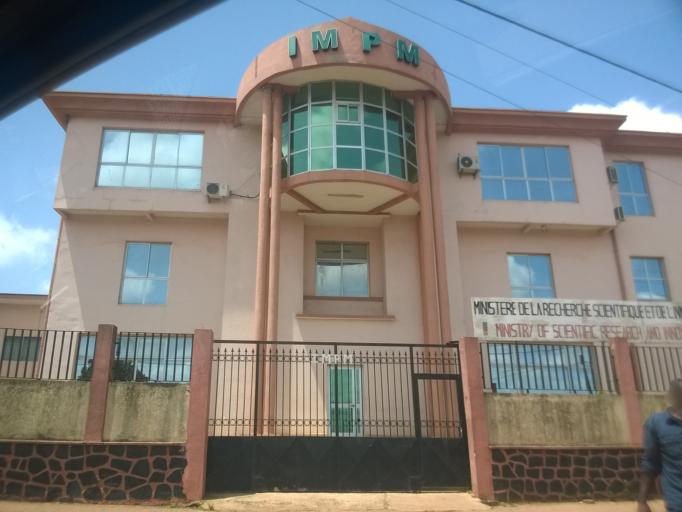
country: CM
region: Centre
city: Yaounde
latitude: 3.8613
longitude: 11.5054
